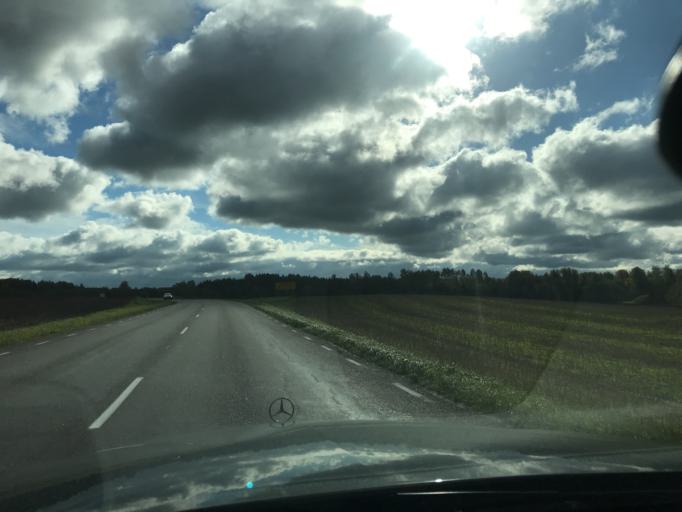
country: EE
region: Vorumaa
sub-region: Antsla vald
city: Vana-Antsla
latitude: 57.9078
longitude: 26.4209
